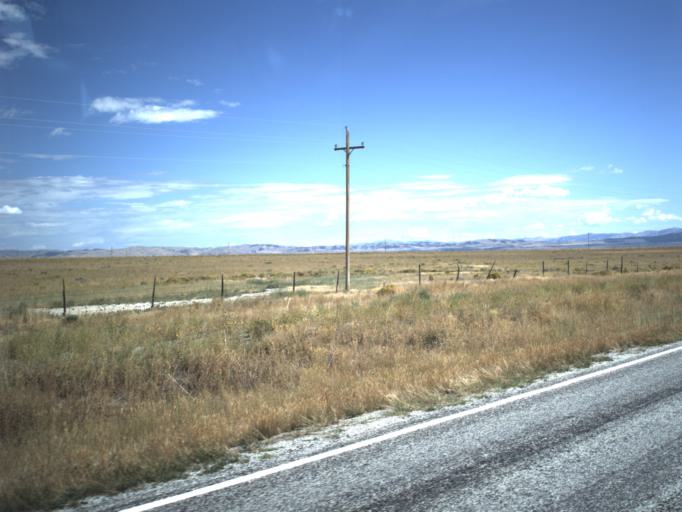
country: US
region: Idaho
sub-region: Oneida County
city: Malad City
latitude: 41.9654
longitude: -113.0457
